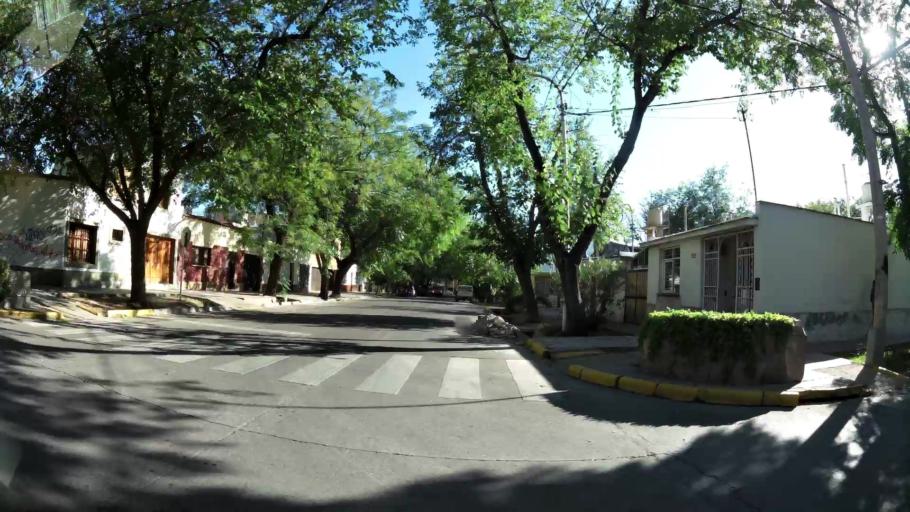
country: AR
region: Mendoza
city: Las Heras
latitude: -32.8662
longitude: -68.8410
